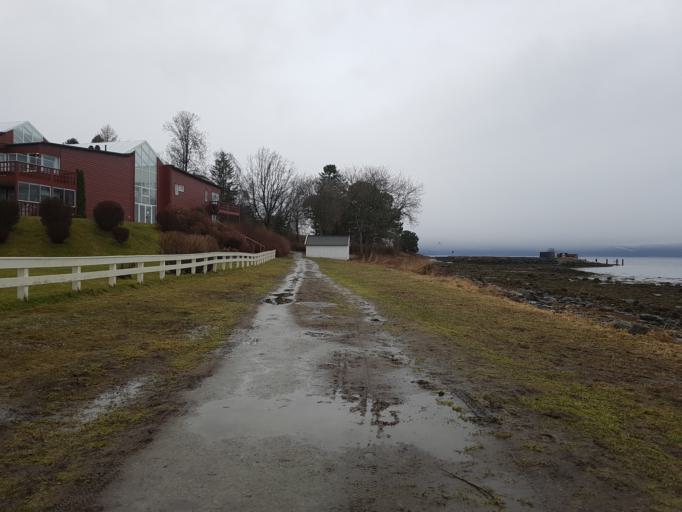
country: NO
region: Sor-Trondelag
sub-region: Trondheim
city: Trondheim
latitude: 63.4366
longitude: 10.4969
